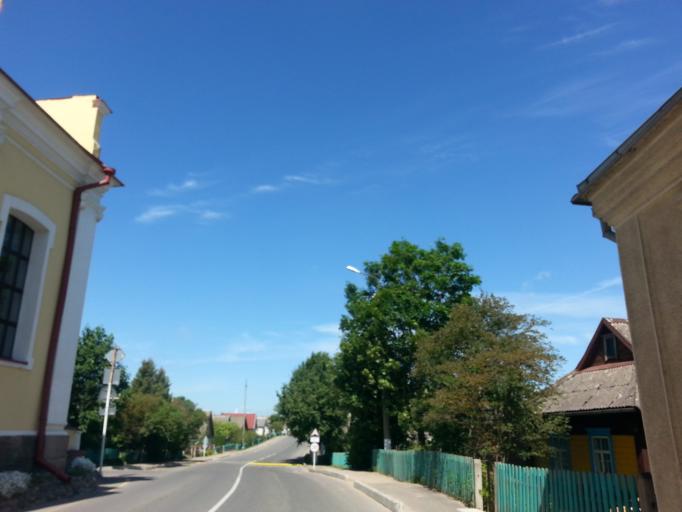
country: BY
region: Vitebsk
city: Hlybokaye
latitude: 55.1412
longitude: 27.6939
